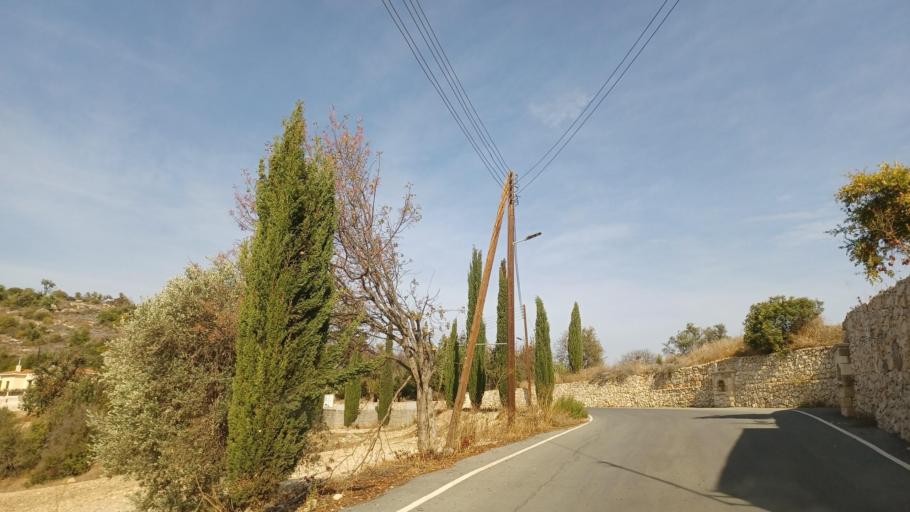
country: CY
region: Pafos
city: Polis
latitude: 34.9740
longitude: 32.5020
